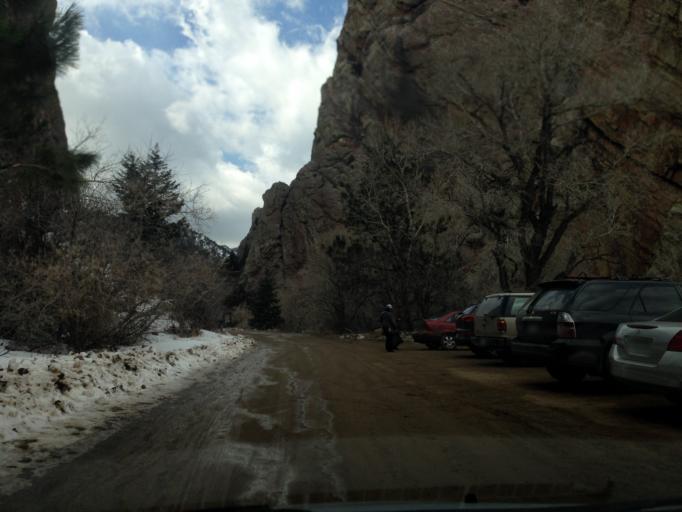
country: US
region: Colorado
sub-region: Boulder County
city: Boulder
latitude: 39.9312
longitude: -105.2816
